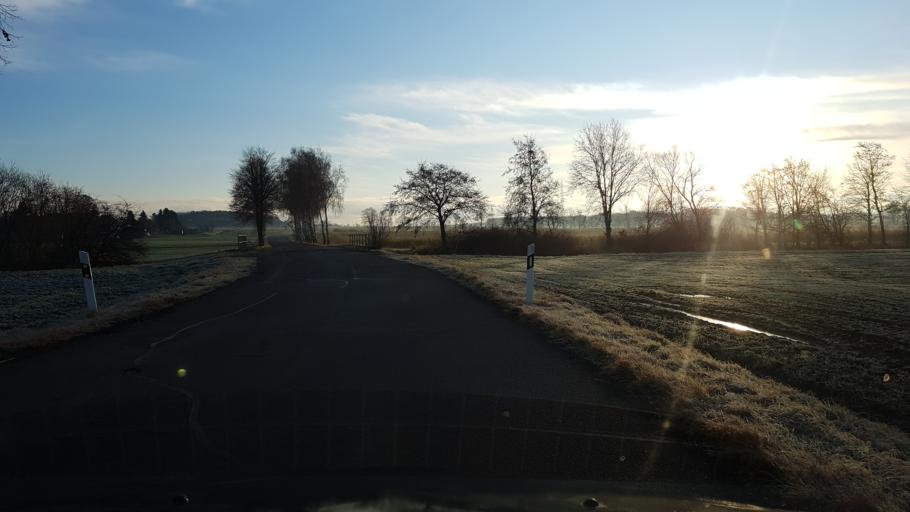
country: DE
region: Saxony
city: Neschwitz
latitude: 51.2437
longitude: 14.3409
